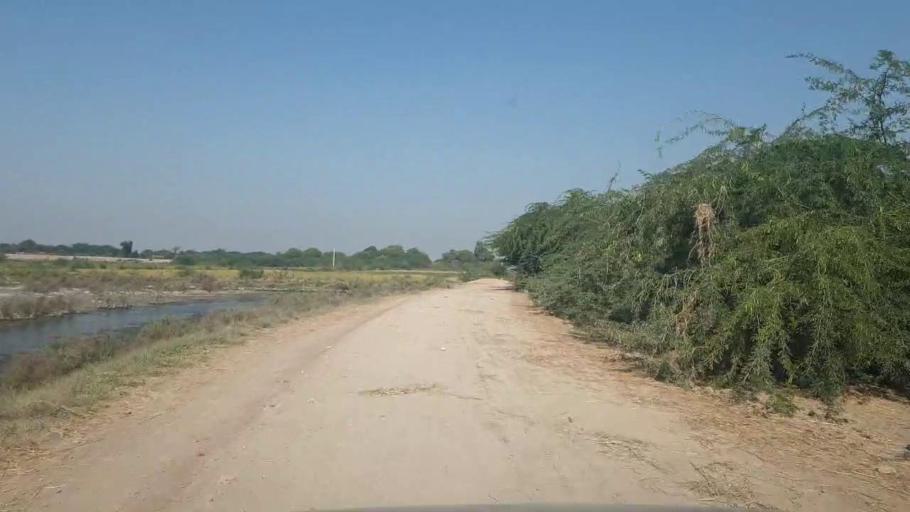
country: PK
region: Sindh
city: Badin
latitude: 24.6756
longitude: 68.8573
